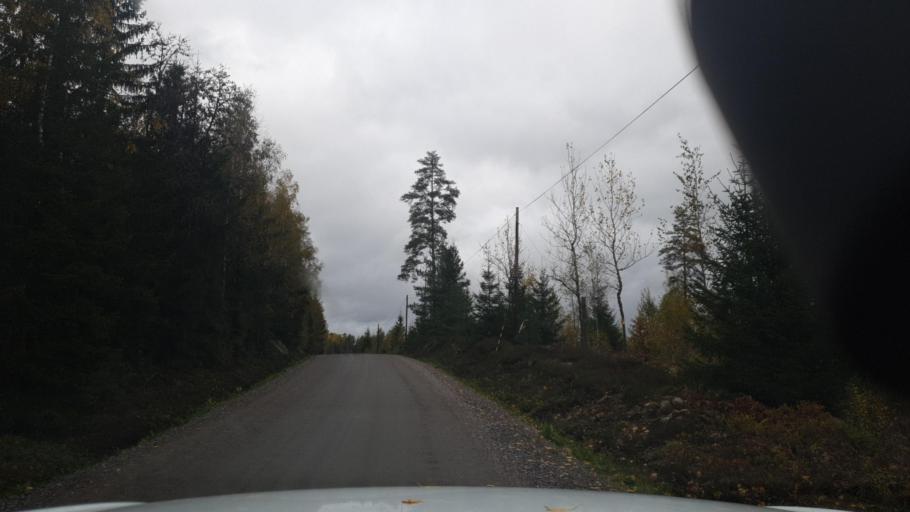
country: SE
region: Vaermland
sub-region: Karlstads Kommun
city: Edsvalla
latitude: 59.5072
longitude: 13.2067
